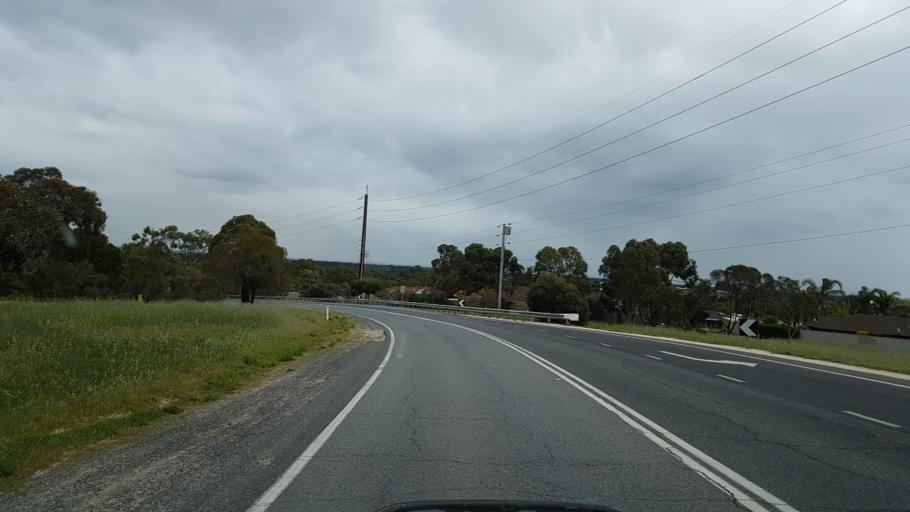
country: AU
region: South Australia
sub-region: Salisbury
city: Elizabeth
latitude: -34.7462
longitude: 138.6845
